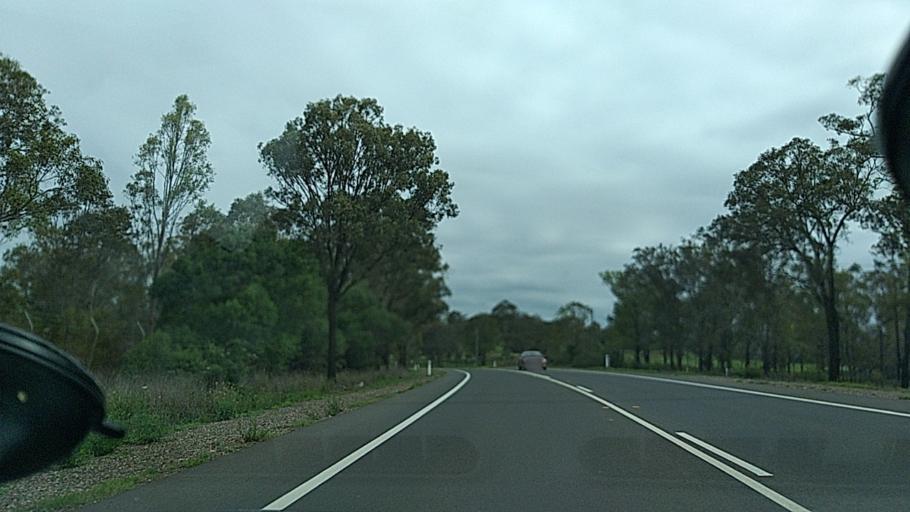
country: AU
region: New South Wales
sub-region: Camden
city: Camden South
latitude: -34.1108
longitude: 150.6964
